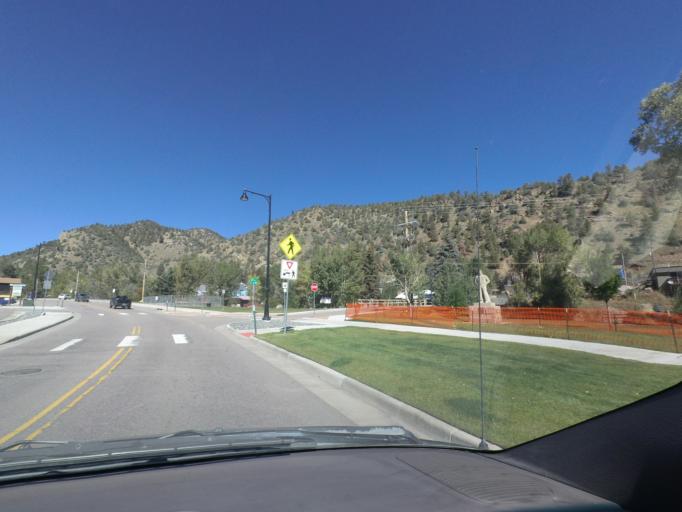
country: US
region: Colorado
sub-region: Clear Creek County
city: Idaho Springs
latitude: 39.7423
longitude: -105.5088
